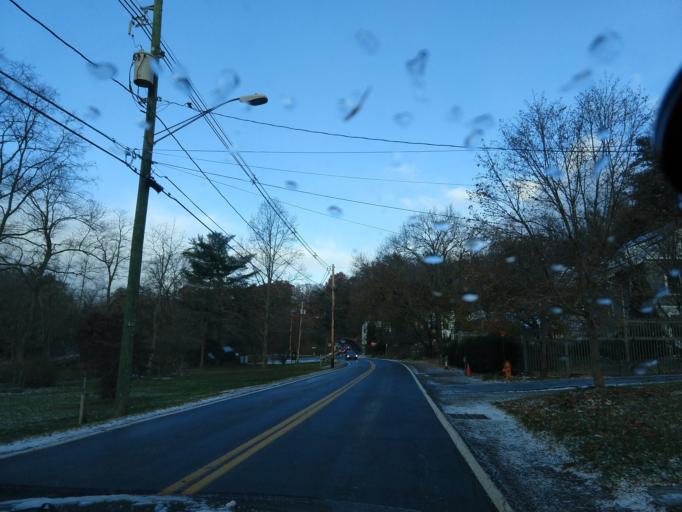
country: US
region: New York
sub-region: Tompkins County
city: East Ithaca
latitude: 42.4526
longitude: -76.4690
